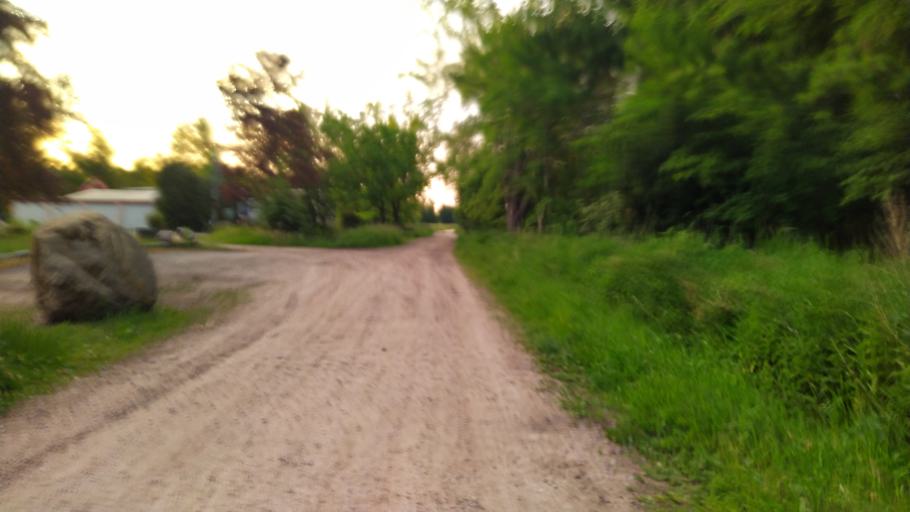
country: DE
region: Lower Saxony
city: Neu Wulmstorf
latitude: 53.4876
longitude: 9.8265
